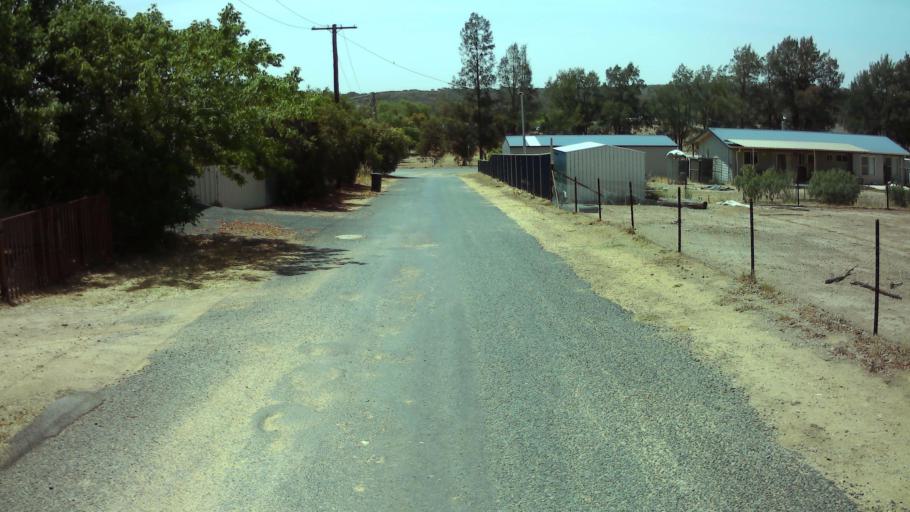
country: AU
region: New South Wales
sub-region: Weddin
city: Grenfell
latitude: -33.8944
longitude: 148.1702
